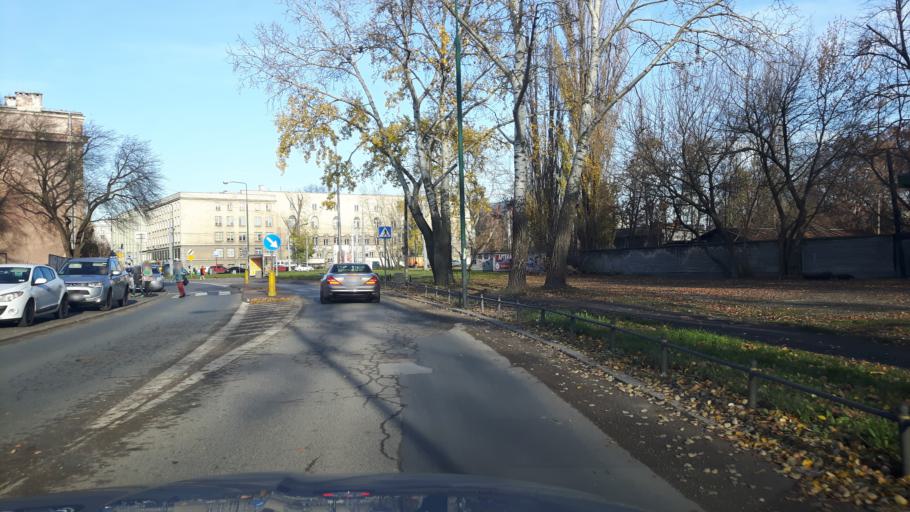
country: PL
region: Masovian Voivodeship
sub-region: Warszawa
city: Ochota
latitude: 52.2092
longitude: 20.9801
